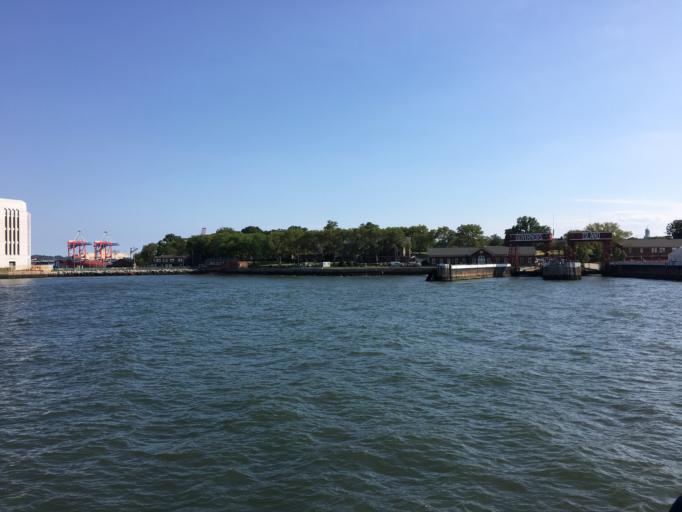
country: US
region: New York
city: New York City
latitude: 40.6952
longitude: -74.0140
